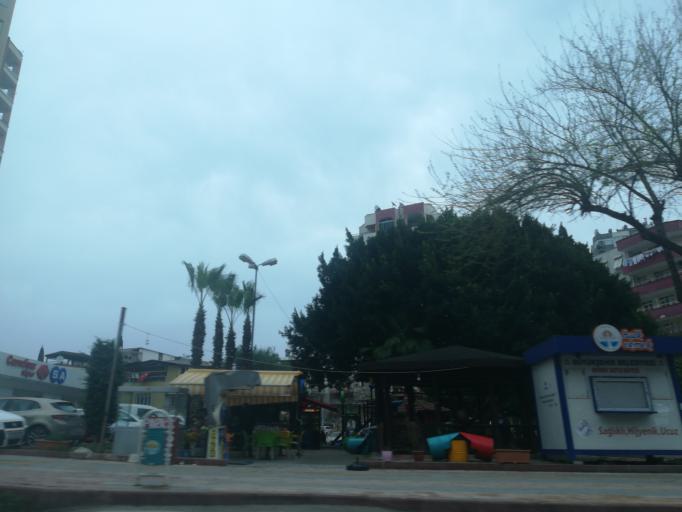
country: TR
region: Adana
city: Adana
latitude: 37.0327
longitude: 35.3091
